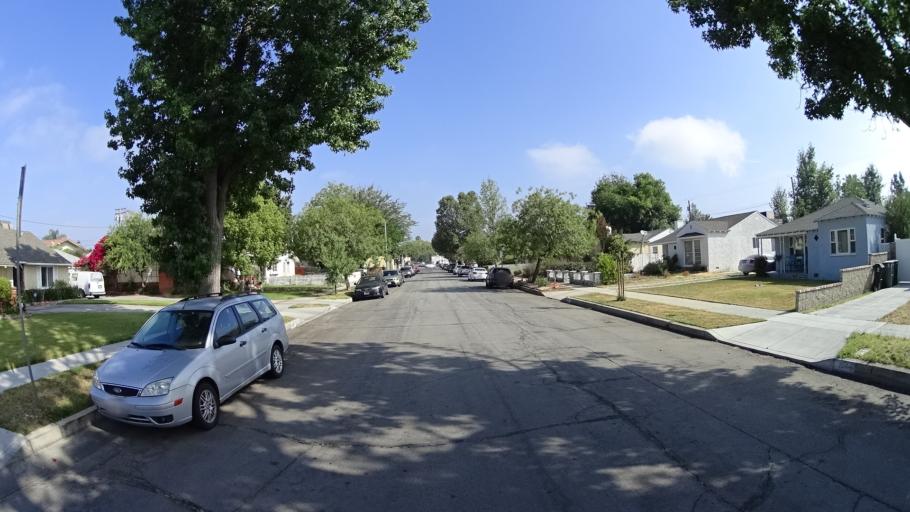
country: US
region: California
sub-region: Los Angeles County
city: Burbank
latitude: 34.1661
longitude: -118.3225
